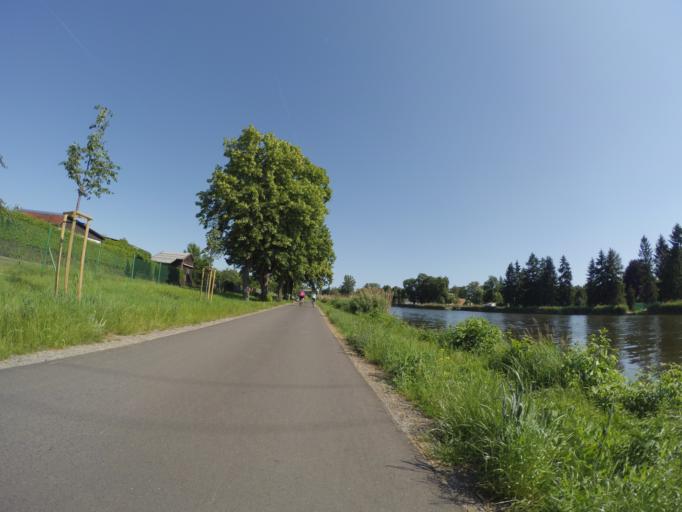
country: CZ
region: Central Bohemia
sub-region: Okres Nymburk
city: Nymburk
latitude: 50.1820
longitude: 15.0565
